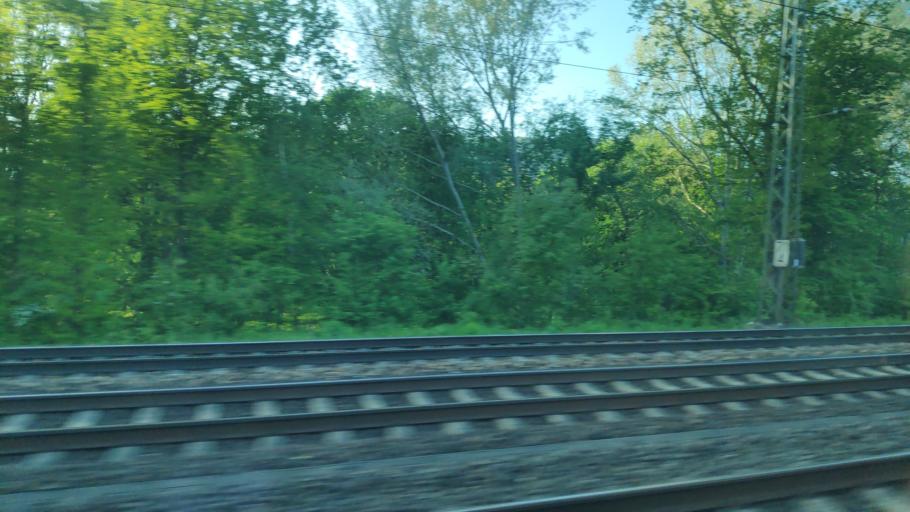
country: DE
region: North Rhine-Westphalia
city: Porta Westfalica
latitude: 52.2336
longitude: 8.9028
